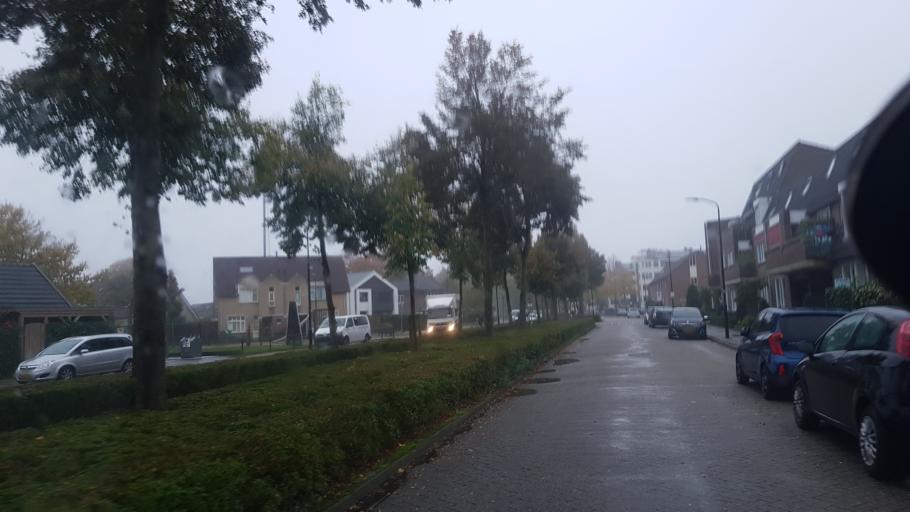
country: NL
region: Gelderland
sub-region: Gemeente Apeldoorn
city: Apeldoorn
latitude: 52.2191
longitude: 5.9461
